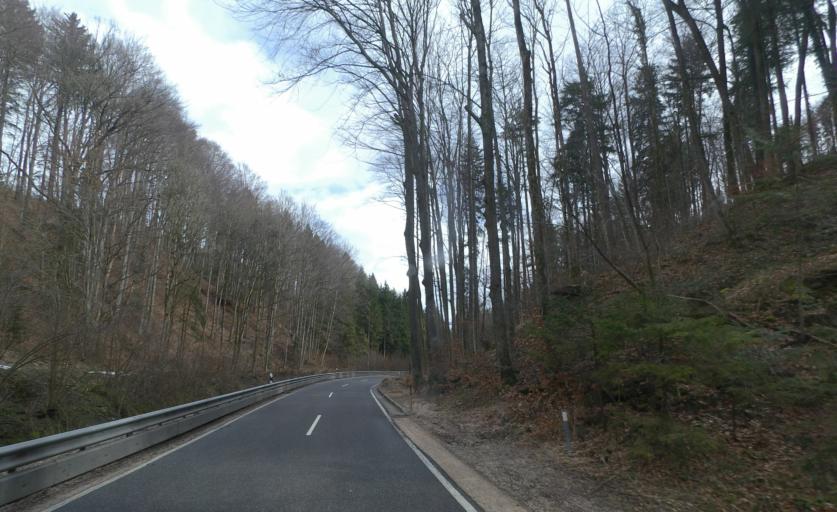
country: DE
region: Bavaria
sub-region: Upper Bavaria
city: Surberg
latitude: 47.8310
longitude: 12.7532
